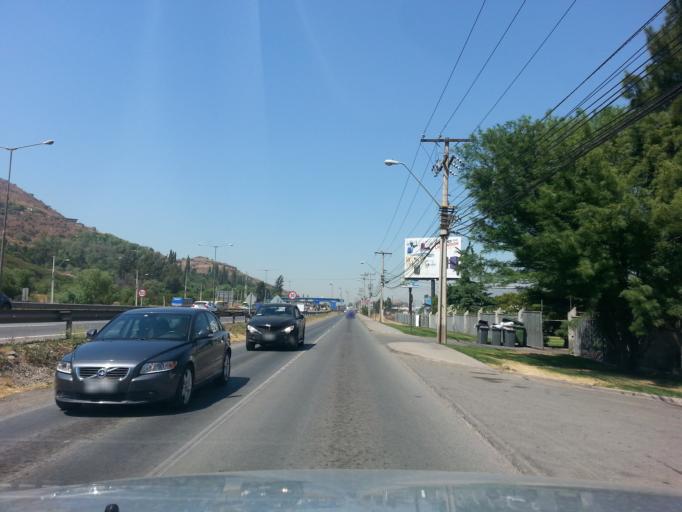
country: CL
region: Santiago Metropolitan
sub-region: Provincia de Chacabuco
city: Chicureo Abajo
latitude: -33.3078
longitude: -70.7007
